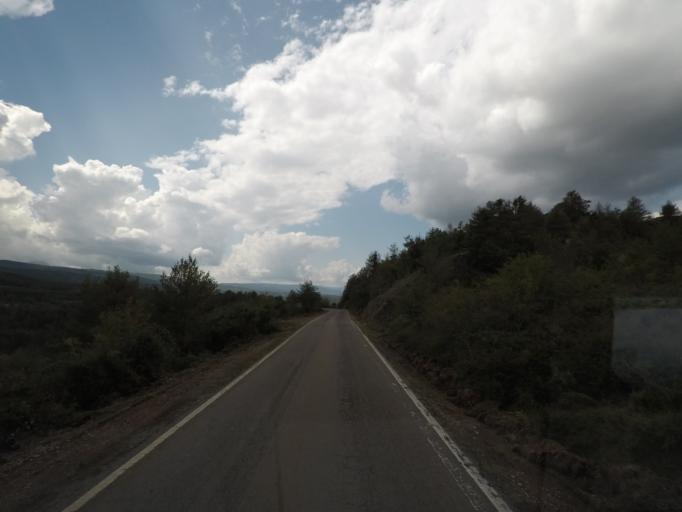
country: ES
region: Aragon
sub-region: Provincia de Huesca
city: Fiscal
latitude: 42.4097
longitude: -0.1060
